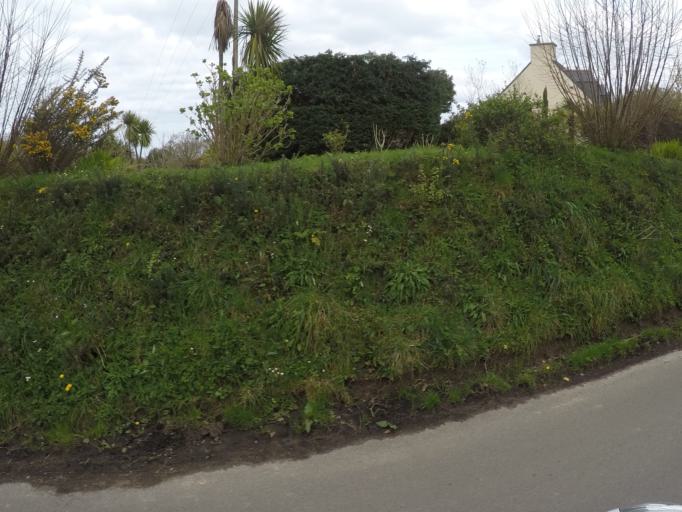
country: FR
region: Brittany
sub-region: Departement des Cotes-d'Armor
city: Plouha
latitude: 48.7028
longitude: -2.9335
